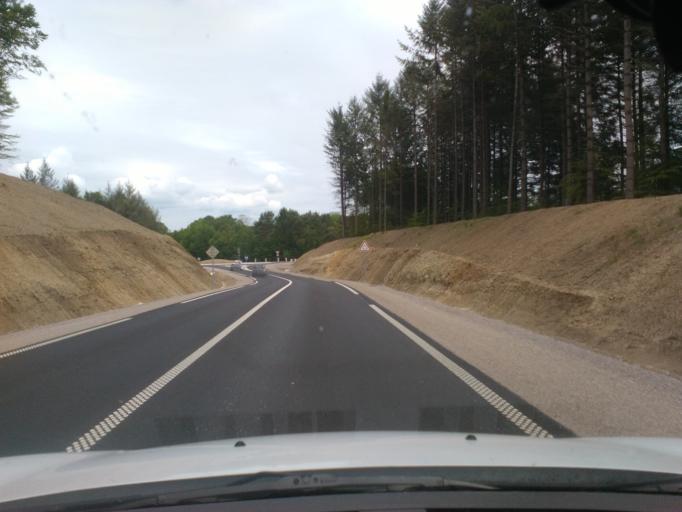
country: FR
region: Lorraine
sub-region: Departement des Vosges
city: Deyvillers
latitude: 48.1811
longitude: 6.4969
